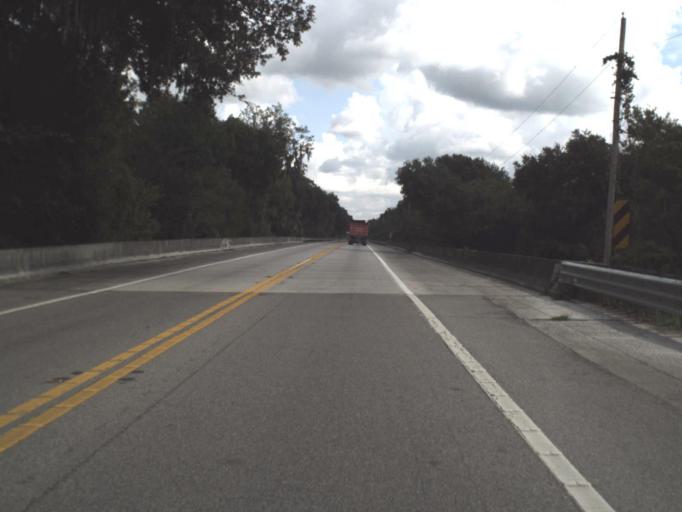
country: US
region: Florida
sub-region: Pasco County
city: Crystal Springs
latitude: 28.1494
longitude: -82.2214
